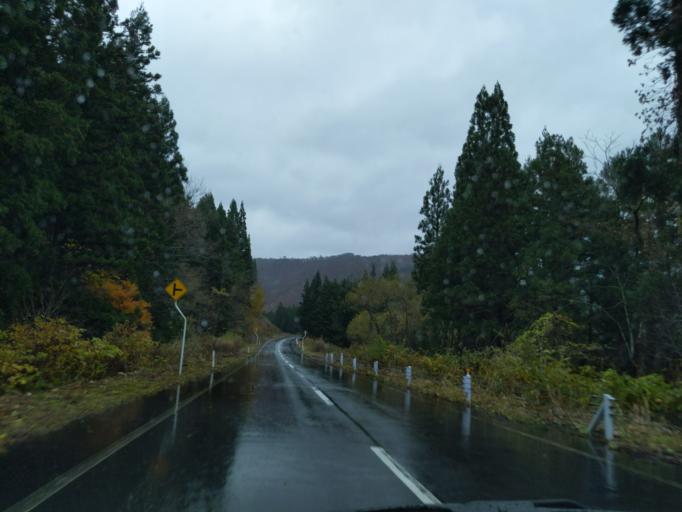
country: JP
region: Iwate
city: Mizusawa
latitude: 39.0618
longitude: 140.8597
